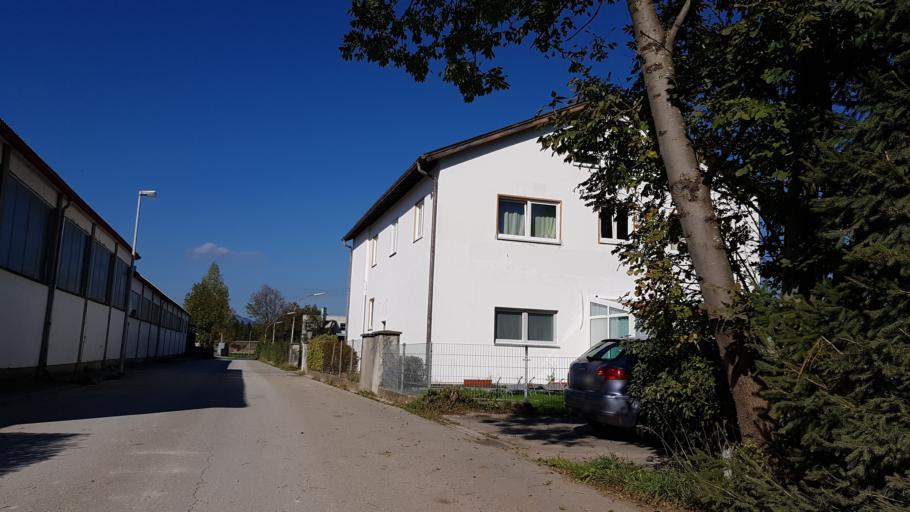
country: DE
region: Bavaria
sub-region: Swabia
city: Fuessen
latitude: 47.5775
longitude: 10.6791
